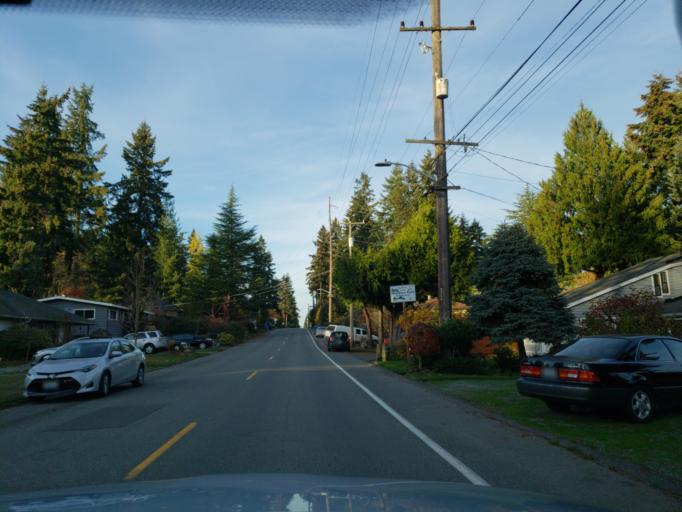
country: US
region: Washington
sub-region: King County
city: Shoreline
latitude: 47.7461
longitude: -122.3400
